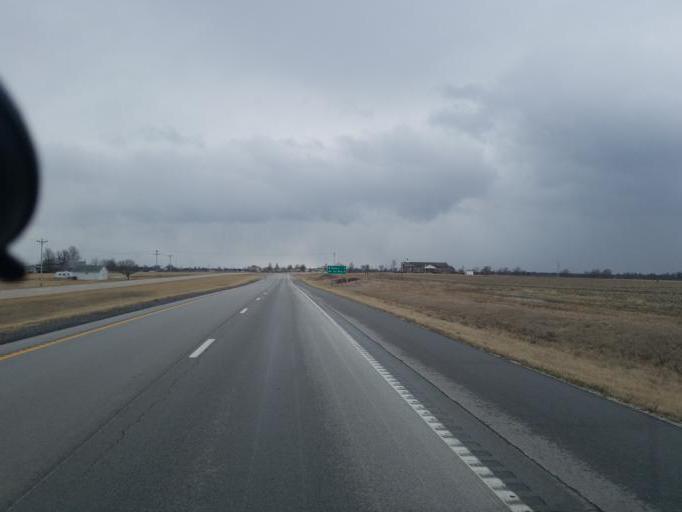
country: US
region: Missouri
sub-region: Macon County
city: Macon
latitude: 39.8049
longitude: -92.4746
